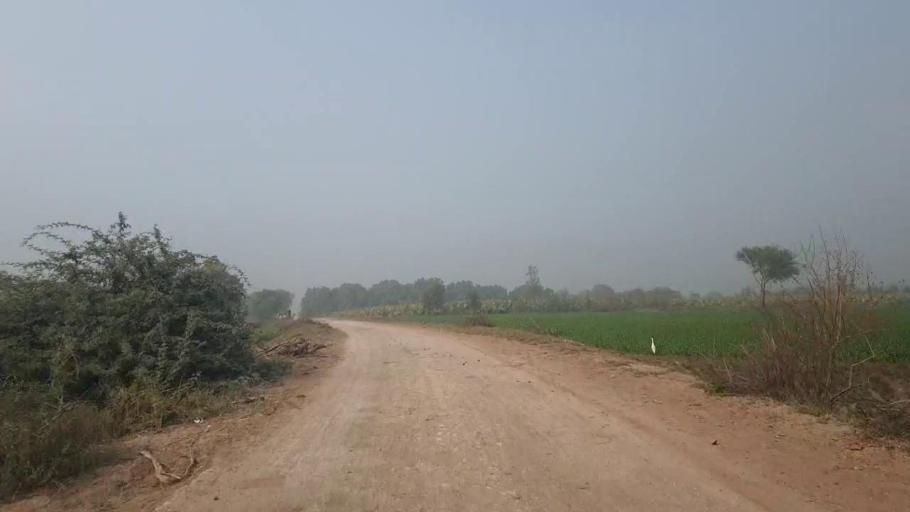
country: PK
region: Sindh
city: Bhit Shah
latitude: 25.8066
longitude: 68.5606
